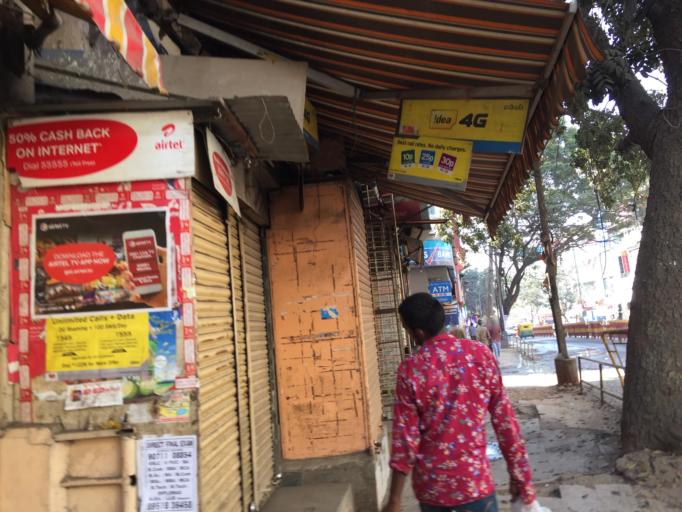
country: IN
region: Karnataka
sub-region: Bangalore Urban
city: Bangalore
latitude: 12.9731
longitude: 77.5773
